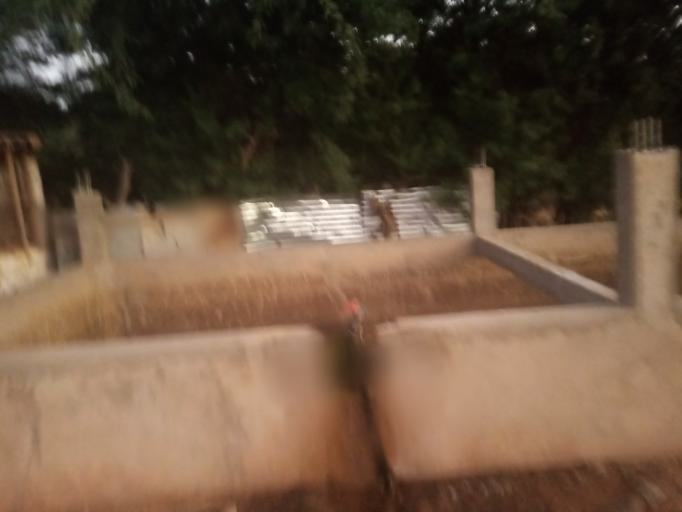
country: SN
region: Saint-Louis
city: Saint-Louis
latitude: 15.9718
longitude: -16.3707
